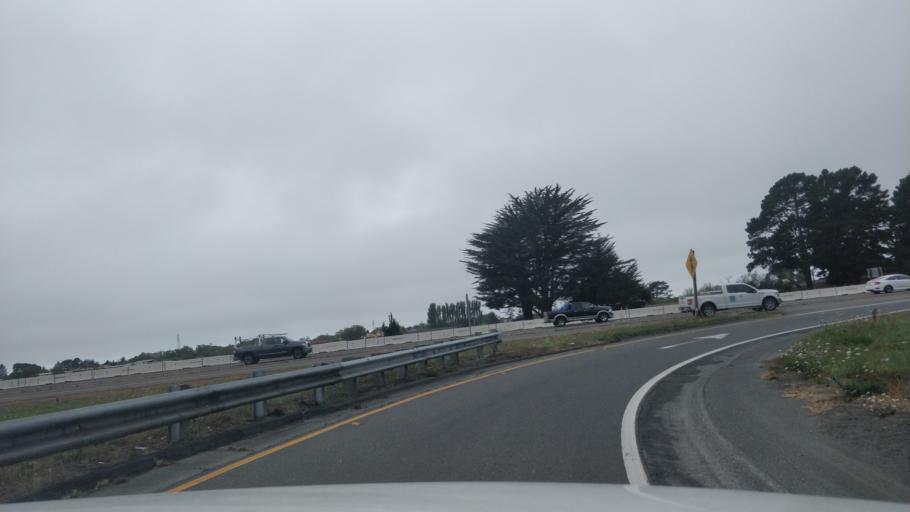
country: US
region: California
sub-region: Humboldt County
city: Arcata
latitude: 40.8617
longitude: -124.0818
